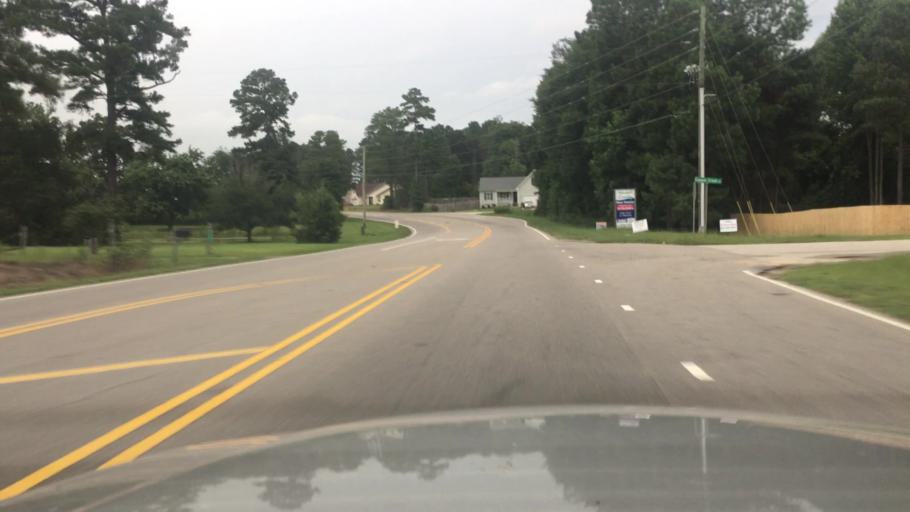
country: US
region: North Carolina
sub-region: Hoke County
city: Rockfish
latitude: 34.9668
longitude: -79.0527
